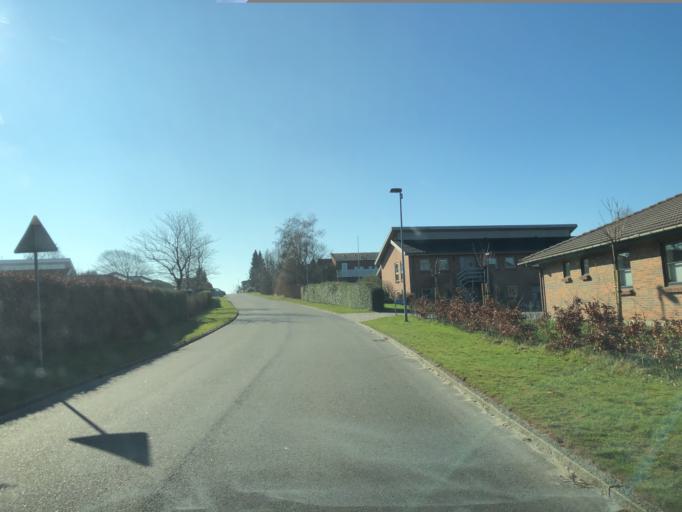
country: DK
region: Central Jutland
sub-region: Ikast-Brande Kommune
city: Bording Kirkeby
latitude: 56.1498
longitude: 9.2792
